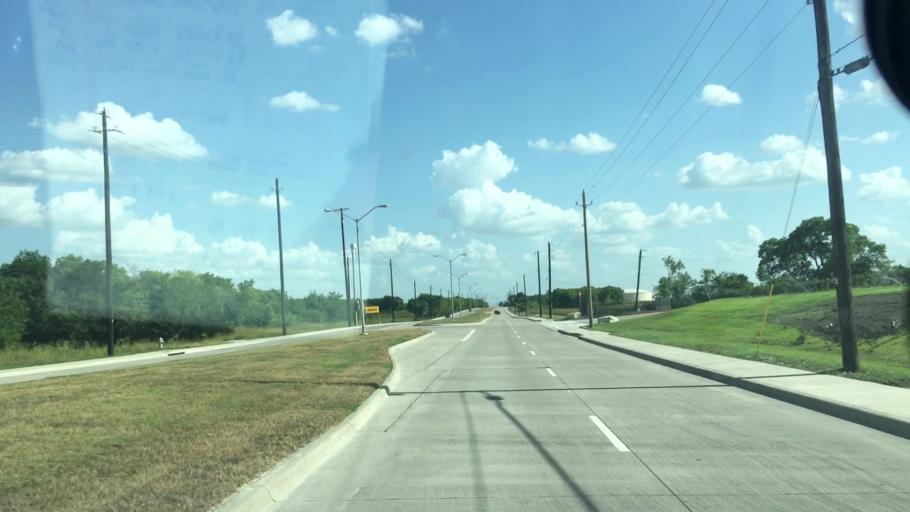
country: US
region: Texas
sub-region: Dallas County
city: Lancaster
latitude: 32.6269
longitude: -96.7528
